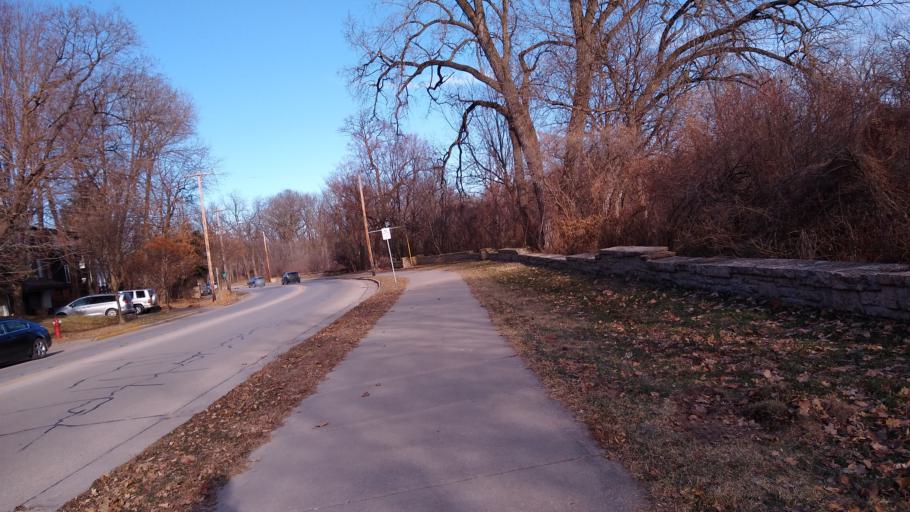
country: US
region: Wisconsin
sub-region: Dane County
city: Shorewood Hills
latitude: 43.0492
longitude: -89.4377
